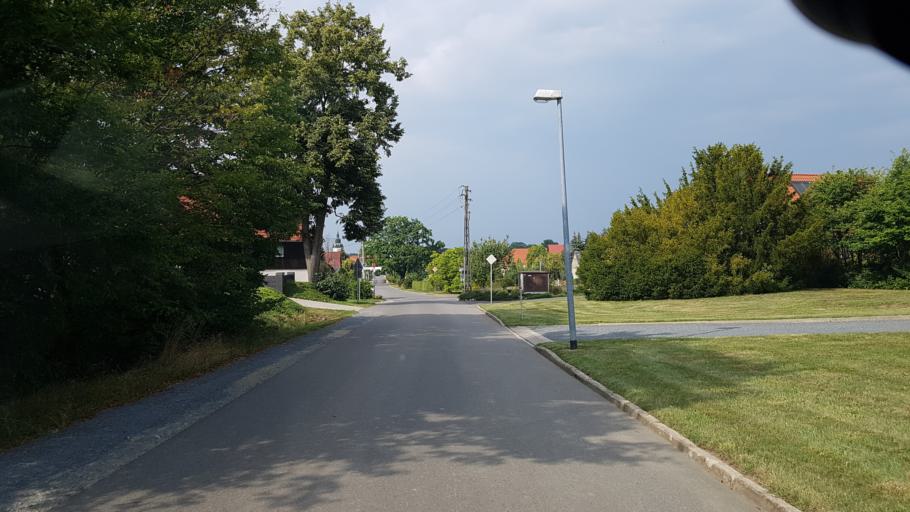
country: DE
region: Brandenburg
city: Grosskmehlen
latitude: 51.3743
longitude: 13.7234
